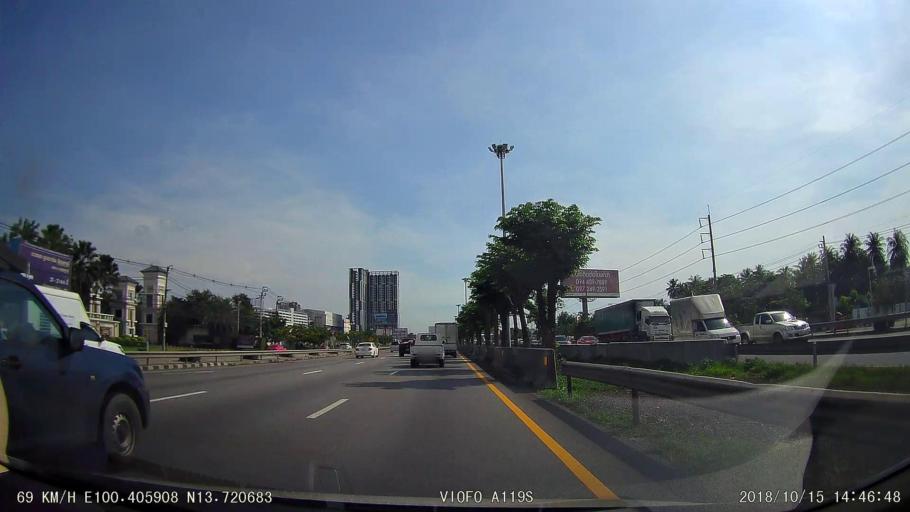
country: TH
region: Bangkok
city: Bang Khae
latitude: 13.7203
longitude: 100.4059
